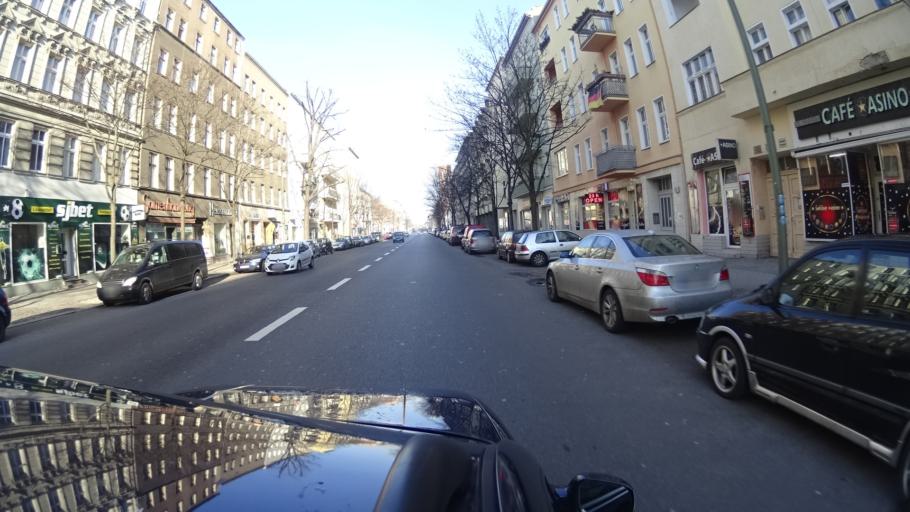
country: DE
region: Berlin
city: Moabit
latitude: 52.5287
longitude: 13.3287
